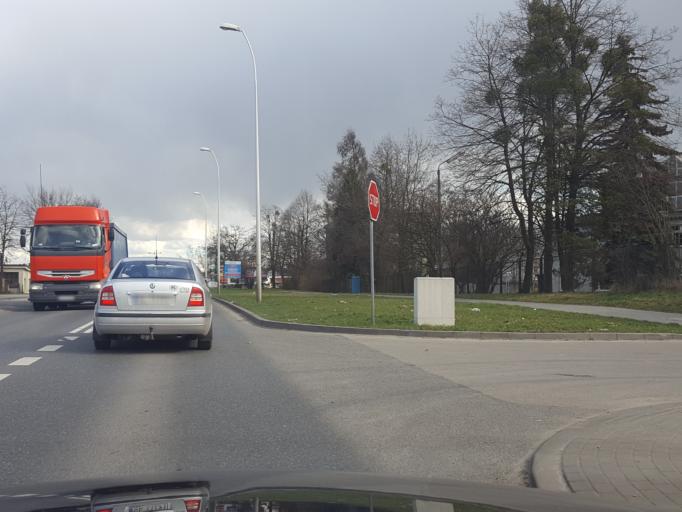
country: PL
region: Silesian Voivodeship
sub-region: Powiat pszczynski
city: Pszczyna
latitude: 49.9672
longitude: 18.9548
